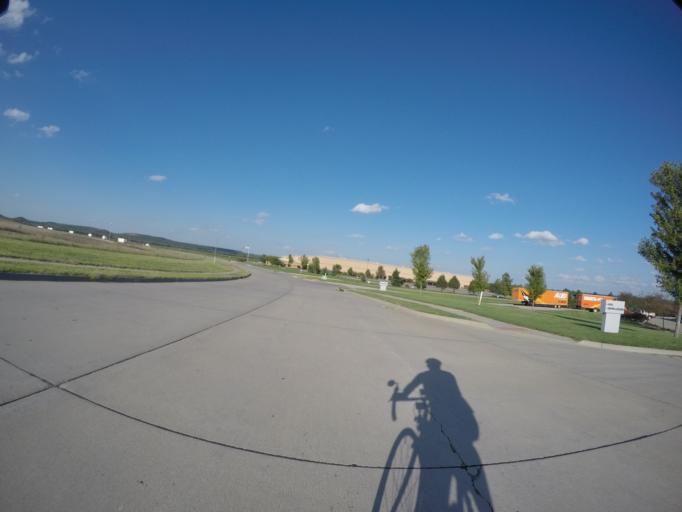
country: US
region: Kansas
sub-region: Riley County
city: Ogden
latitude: 39.1398
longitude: -96.6780
